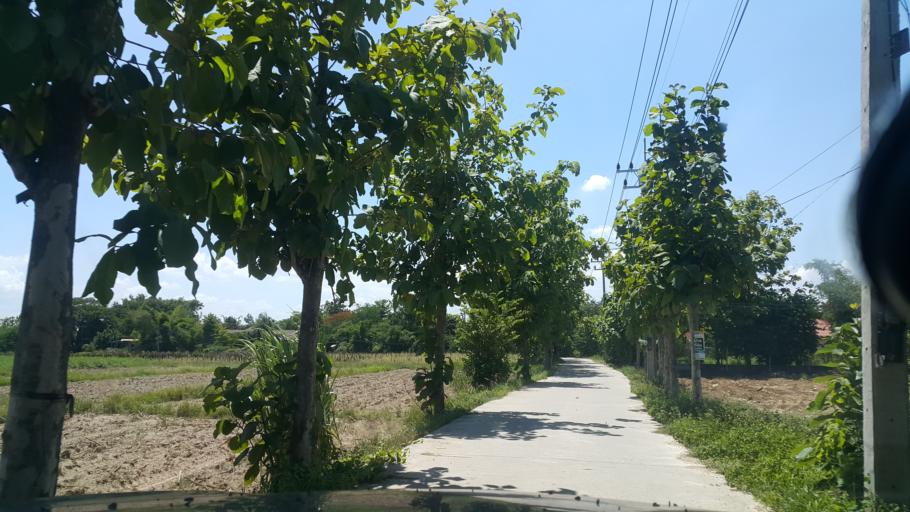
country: TH
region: Chiang Mai
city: San Kamphaeng
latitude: 18.7013
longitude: 99.1488
